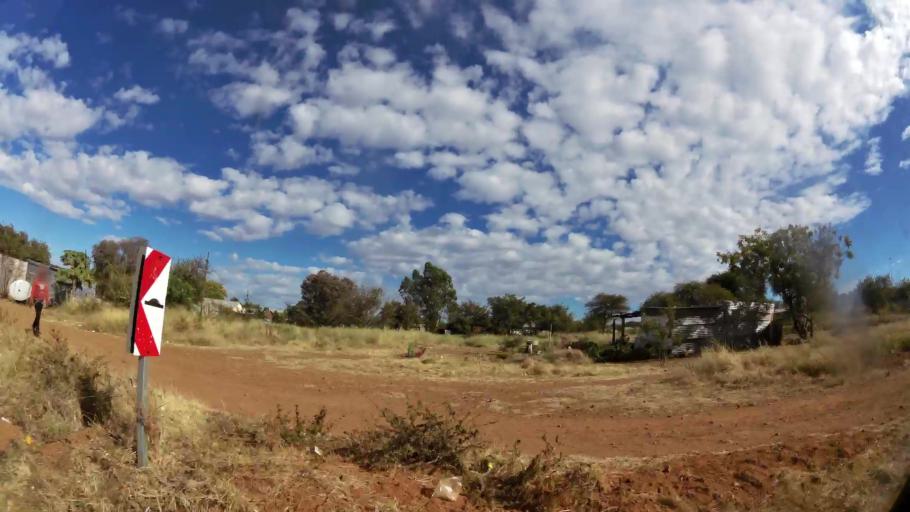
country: ZA
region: Limpopo
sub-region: Waterberg District Municipality
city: Warmbaths
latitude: -24.8756
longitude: 28.2734
